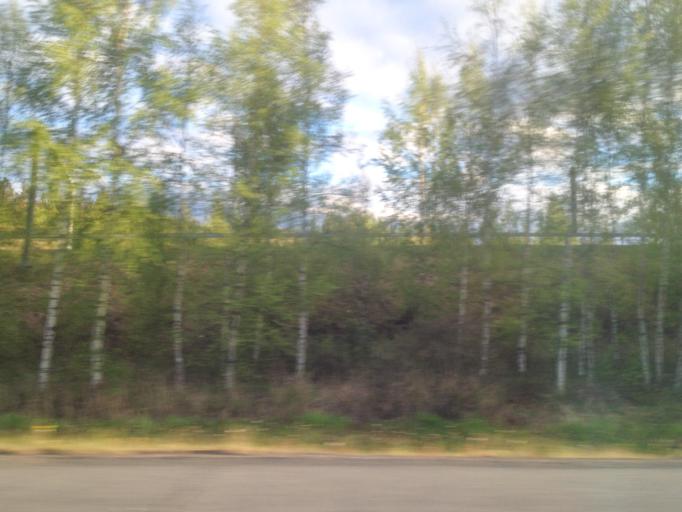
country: FI
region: Pirkanmaa
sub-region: Etelae-Pirkanmaa
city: Akaa
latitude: 61.1817
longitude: 23.8912
